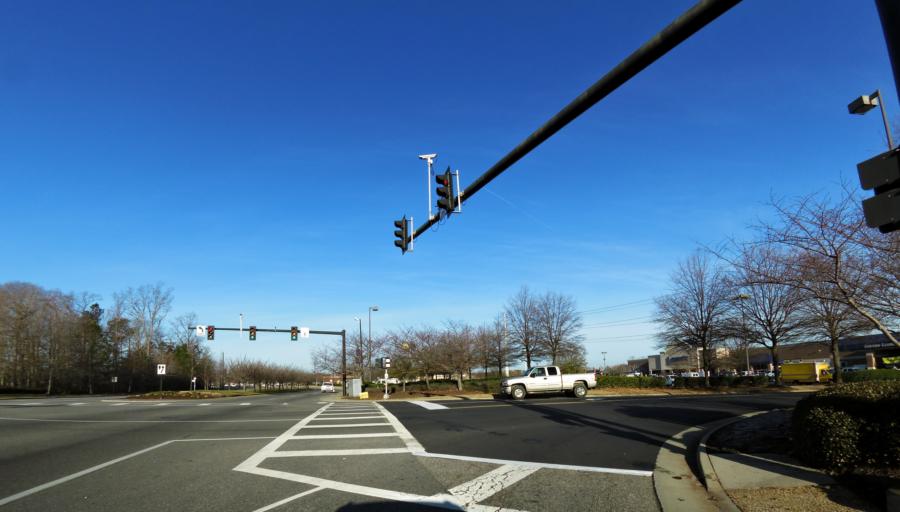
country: US
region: Virginia
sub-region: City of Hampton
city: Hampton
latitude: 37.0365
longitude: -76.3968
